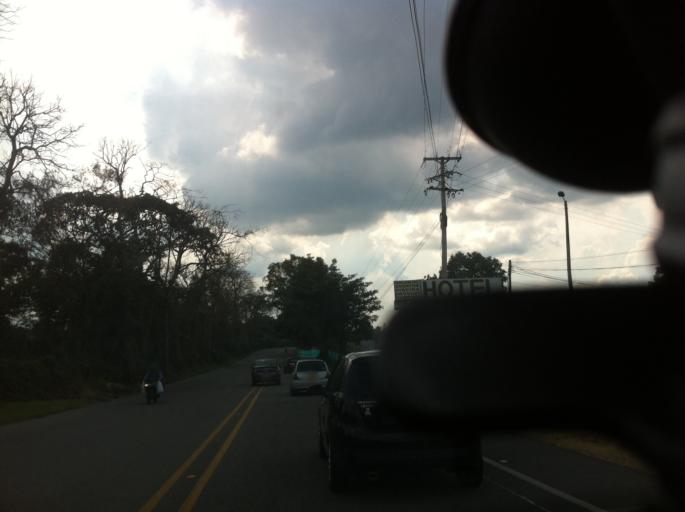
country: CO
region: Quindio
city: La Tebaida
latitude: 4.4938
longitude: -75.7359
